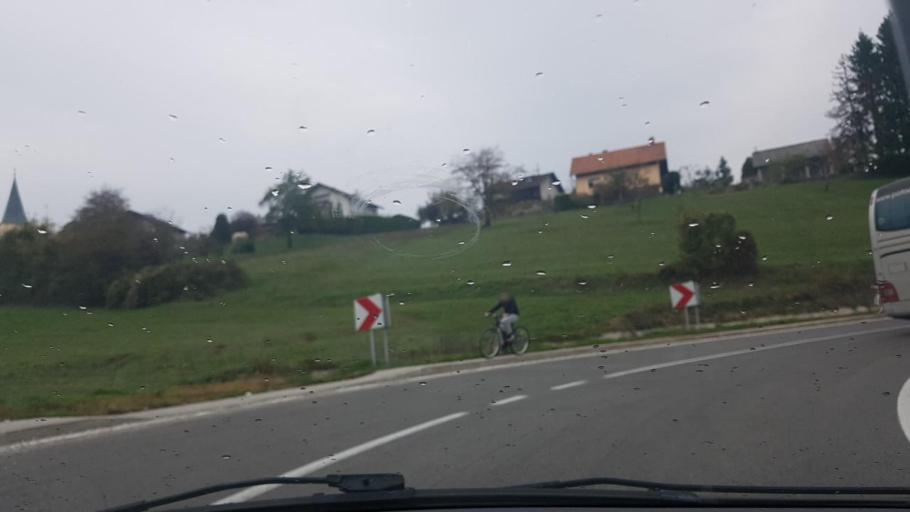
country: SI
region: Rogatec
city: Rogatec
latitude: 46.2103
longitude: 15.6871
